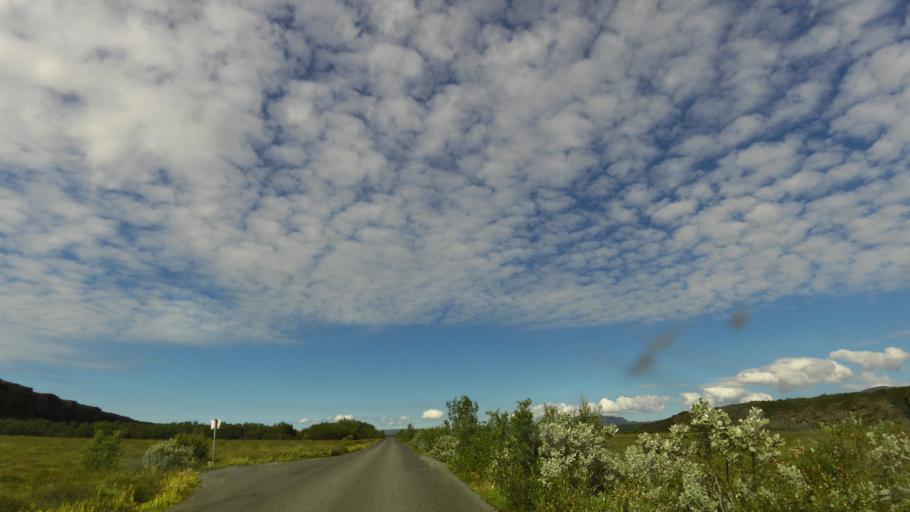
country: IS
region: Northeast
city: Husavik
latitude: 66.0212
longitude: -16.4957
